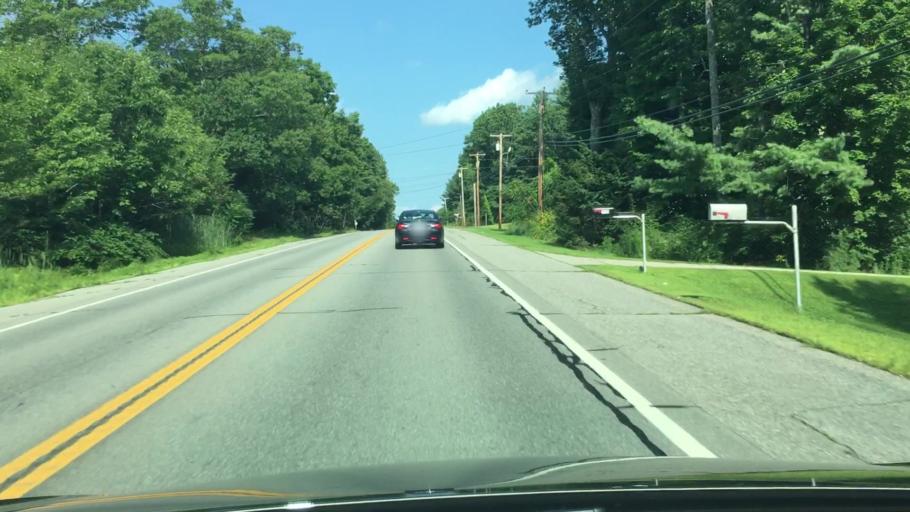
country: US
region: Maine
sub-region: Kennebec County
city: Augusta
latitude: 44.3331
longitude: -69.7109
